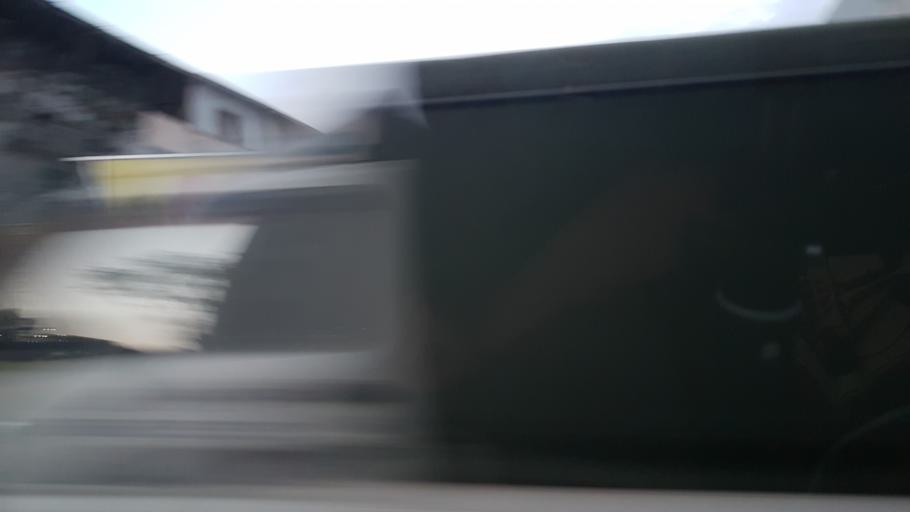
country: TW
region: Taiwan
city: Xinying
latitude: 23.3073
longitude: 120.3034
